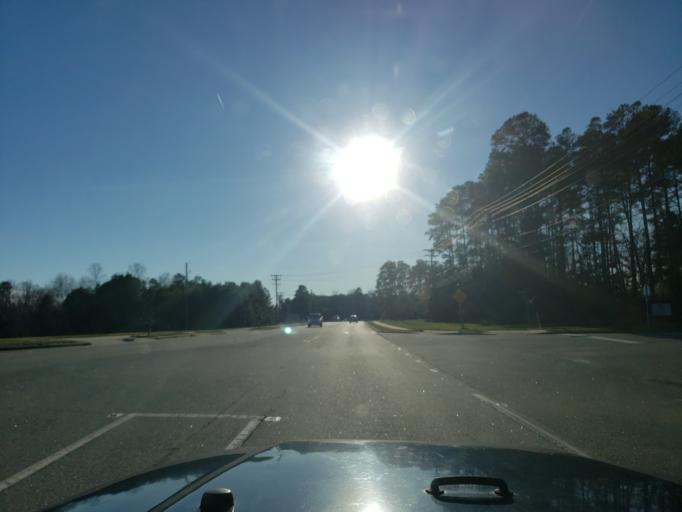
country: US
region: North Carolina
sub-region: Catawba County
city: Lake Norman of Catawba
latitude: 35.5566
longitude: -80.9224
